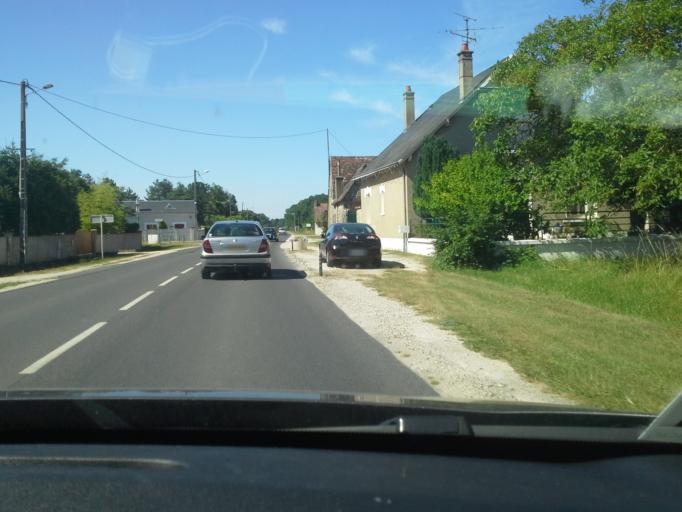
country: FR
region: Centre
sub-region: Departement du Loir-et-Cher
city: Cormeray
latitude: 47.4938
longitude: 1.4056
